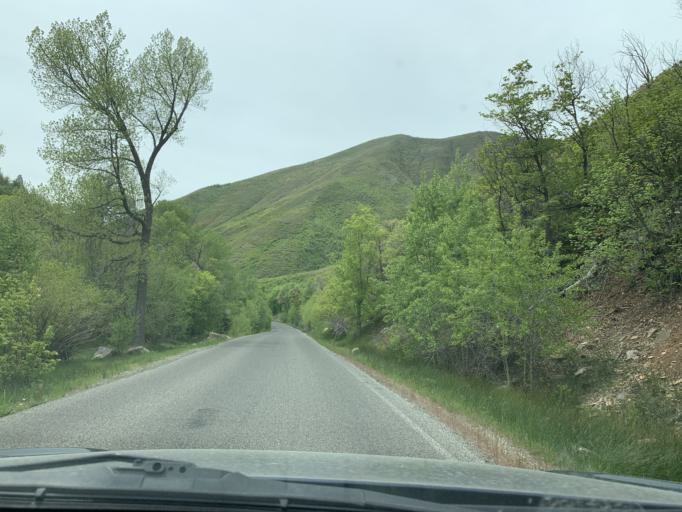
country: US
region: Utah
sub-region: Utah County
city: Mapleton
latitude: 40.1829
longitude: -111.4657
